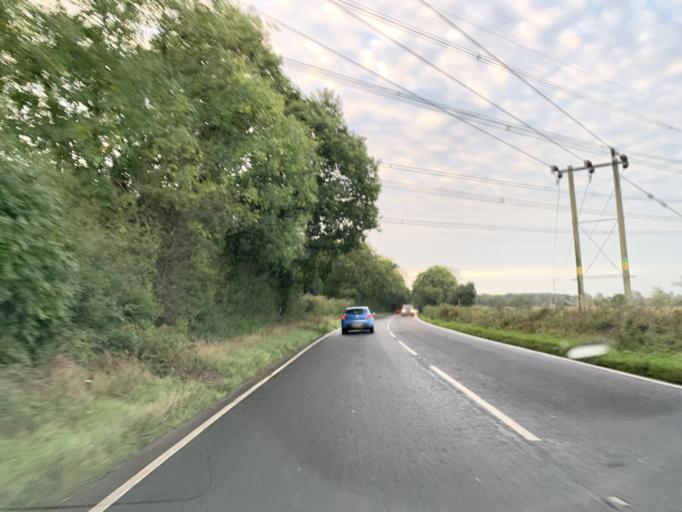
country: GB
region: England
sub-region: Hampshire
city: Romsey
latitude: 50.9614
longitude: -1.4745
